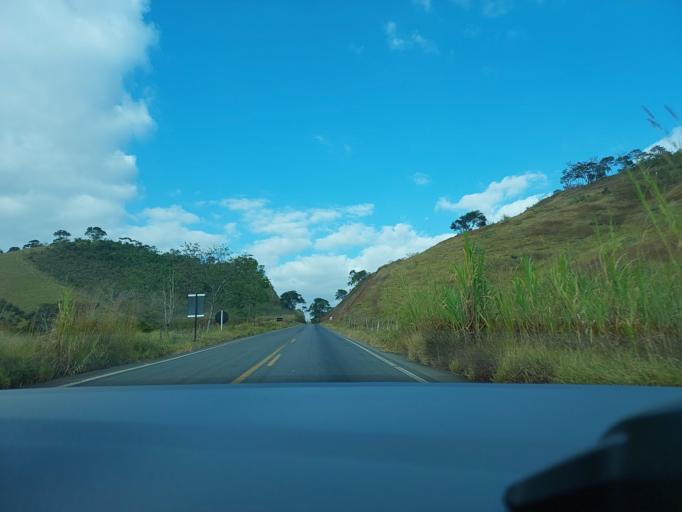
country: BR
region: Minas Gerais
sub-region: Vicosa
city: Vicosa
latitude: -20.8399
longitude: -42.7145
